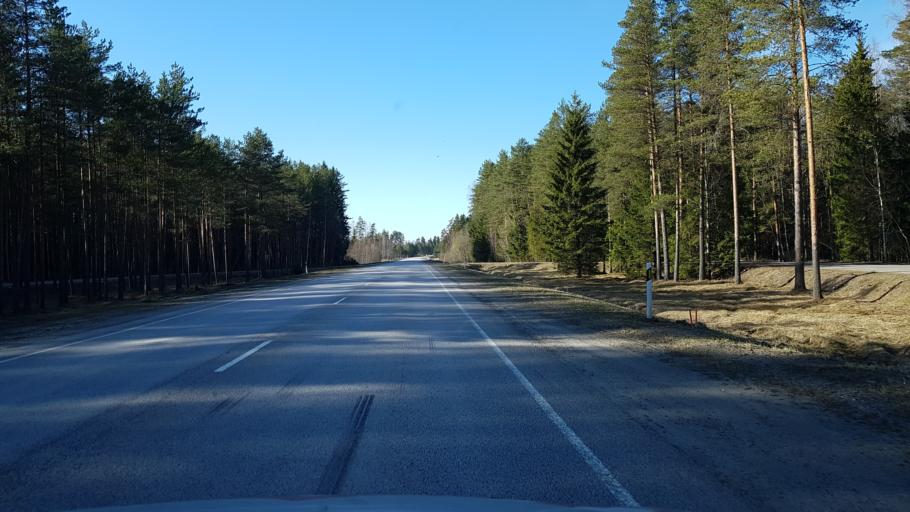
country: EE
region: Ida-Virumaa
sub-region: Johvi vald
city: Johvi
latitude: 59.1562
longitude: 27.3572
